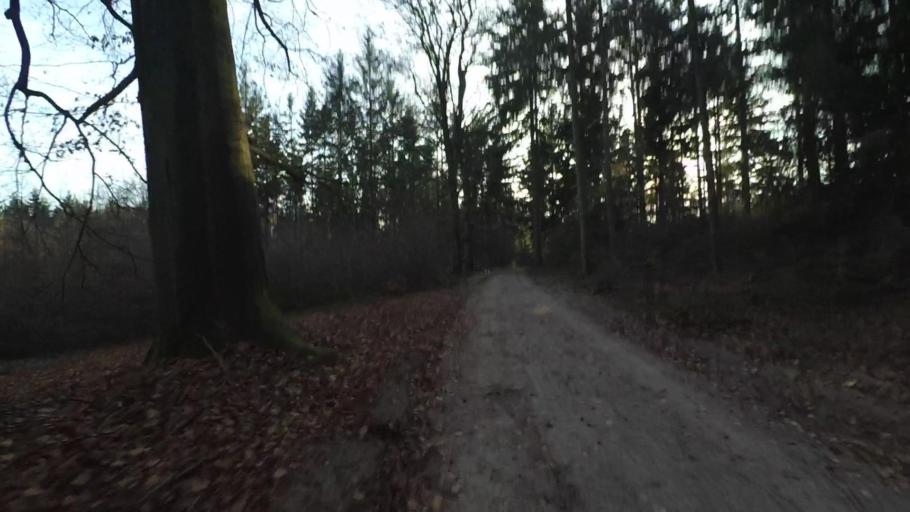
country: NL
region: Utrecht
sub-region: Gemeente Utrechtse Heuvelrug
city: Maarn
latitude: 52.0752
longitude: 5.3477
